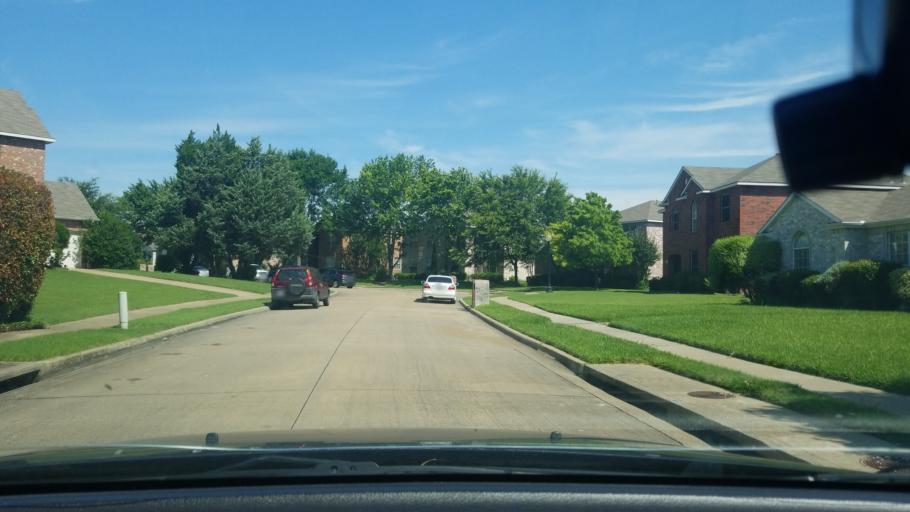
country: US
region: Texas
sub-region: Dallas County
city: Mesquite
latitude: 32.7722
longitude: -96.5882
